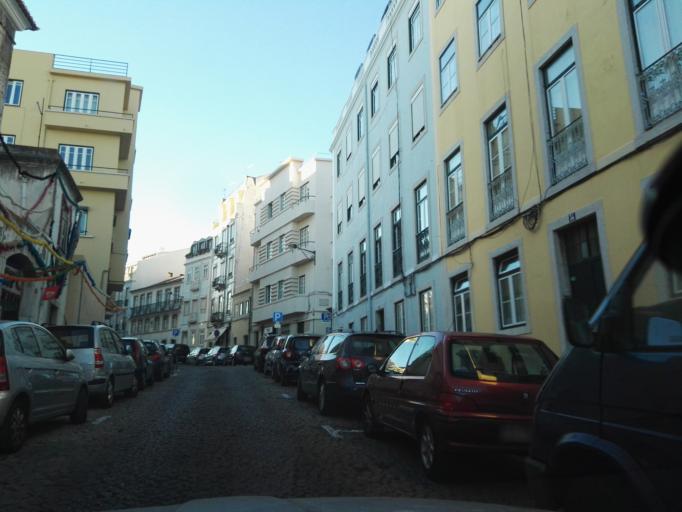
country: PT
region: Setubal
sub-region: Almada
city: Cacilhas
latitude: 38.7089
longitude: -9.1573
